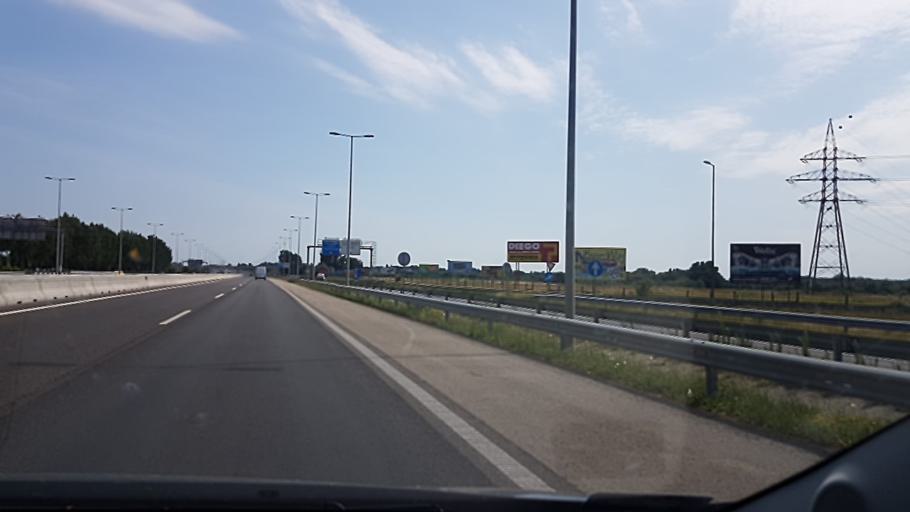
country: HU
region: Budapest
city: Budapest XIX. keruelet
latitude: 47.4215
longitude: 19.1527
